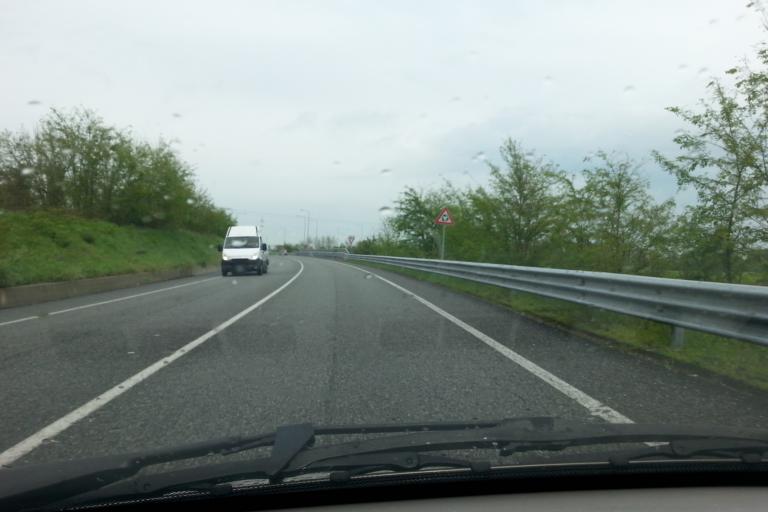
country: IT
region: Piedmont
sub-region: Provincia di Torino
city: San Gillio
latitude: 45.1205
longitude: 7.5290
